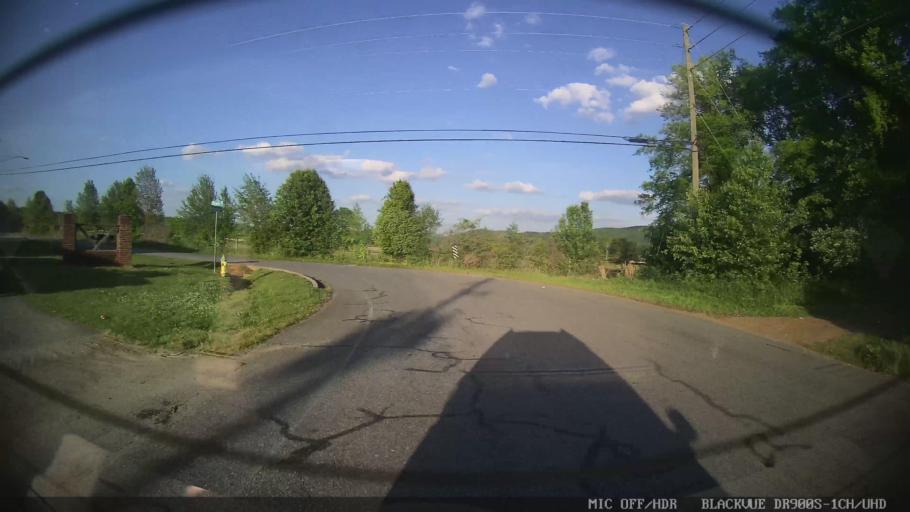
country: US
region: Georgia
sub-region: Bartow County
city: Cartersville
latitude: 34.1460
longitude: -84.7939
